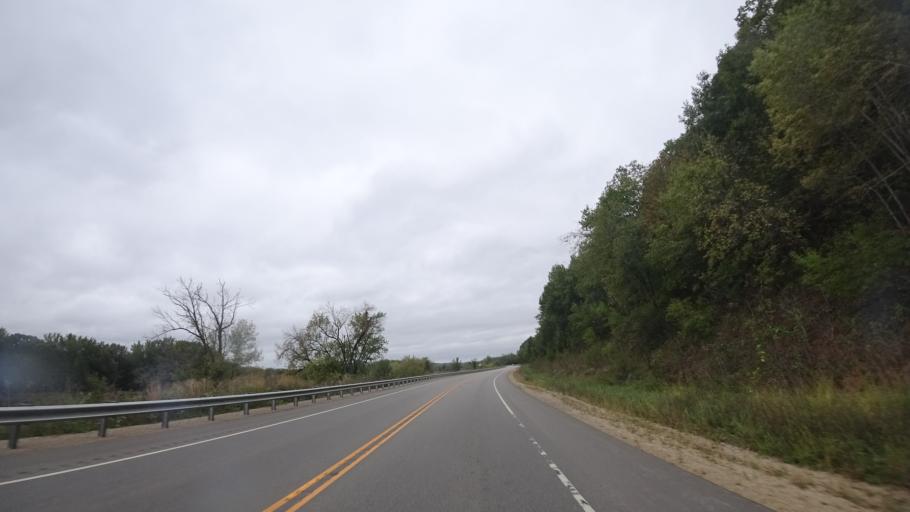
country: US
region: Wisconsin
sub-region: Grant County
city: Boscobel
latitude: 43.1632
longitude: -90.7059
